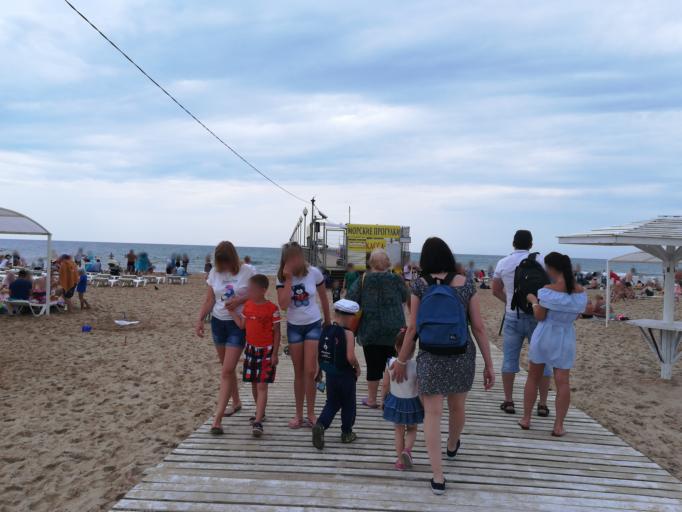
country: RU
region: Krasnodarskiy
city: Vityazevo
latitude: 44.9823
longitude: 37.2487
